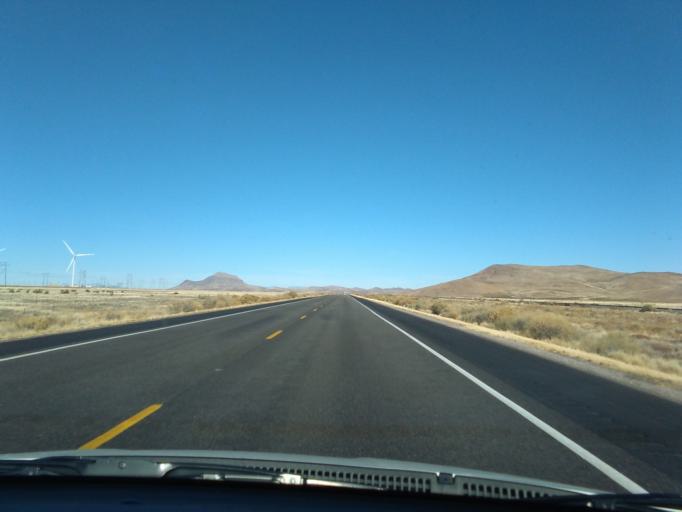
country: US
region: New Mexico
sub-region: Luna County
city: Deming
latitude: 32.5206
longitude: -107.4972
